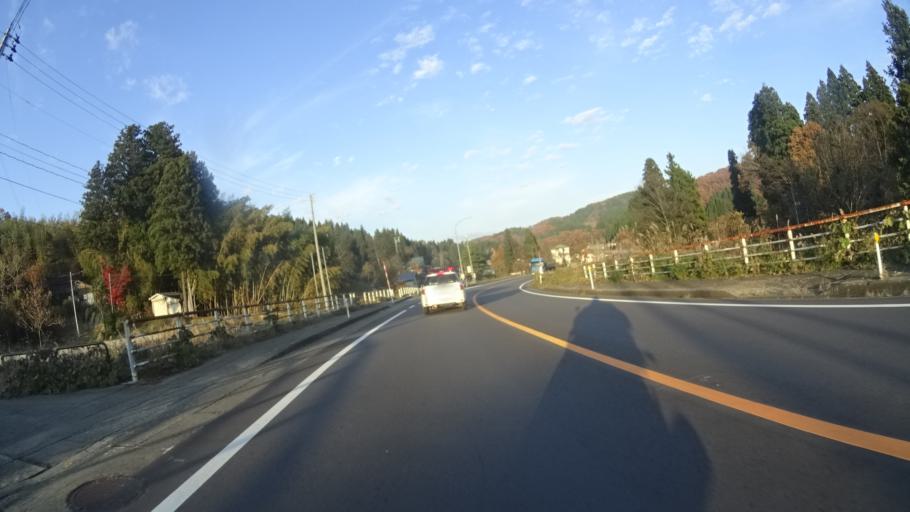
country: JP
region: Niigata
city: Nagaoka
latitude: 37.4192
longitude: 138.7204
